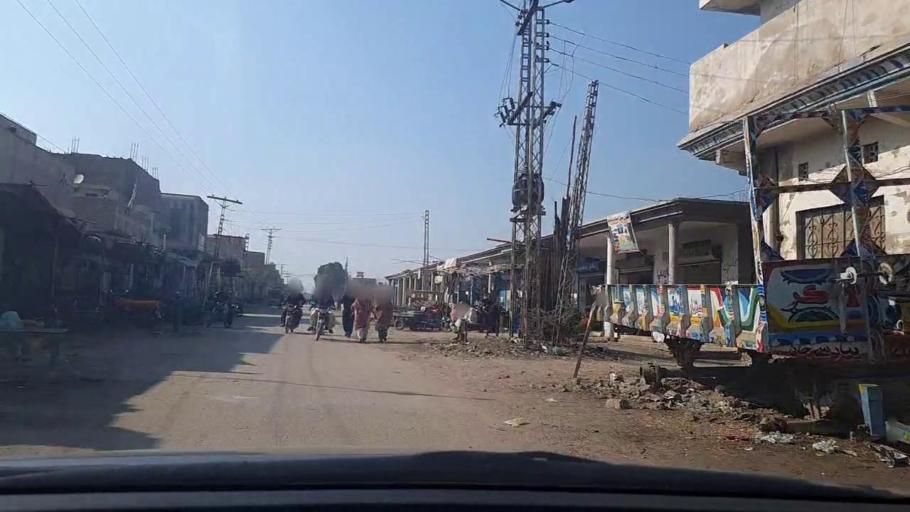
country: PK
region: Sindh
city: Daulatpur
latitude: 26.3024
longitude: 68.0985
